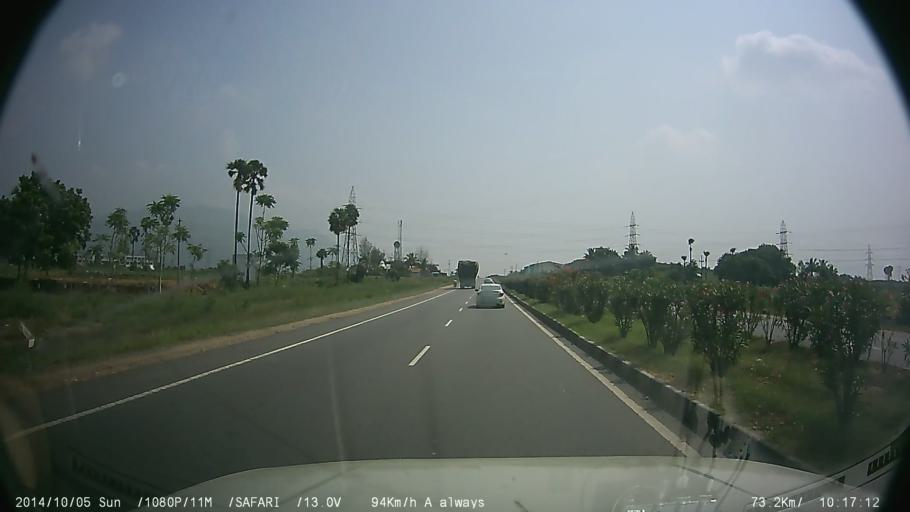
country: IN
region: Tamil Nadu
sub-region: Salem
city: Attayyampatti
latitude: 11.5722
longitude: 78.0363
